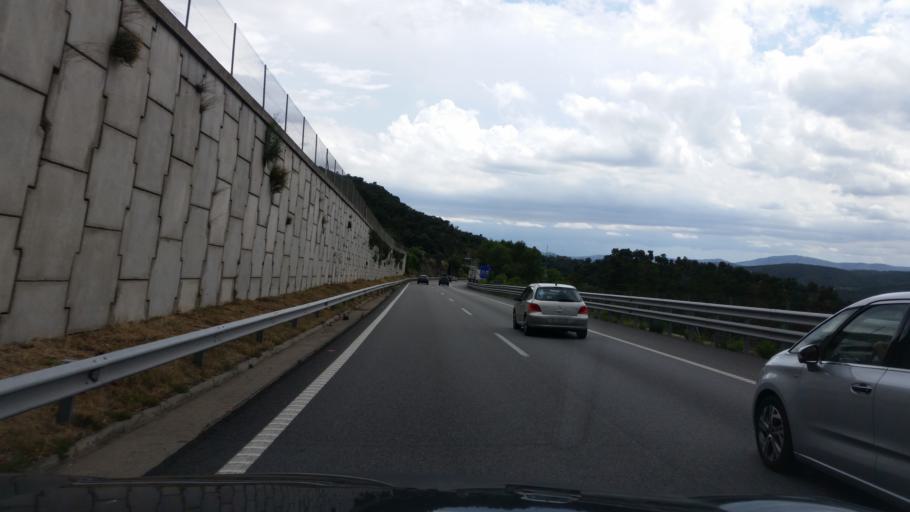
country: ES
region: Catalonia
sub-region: Provincia de Girona
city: la Jonquera
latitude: 42.4520
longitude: 2.8677
